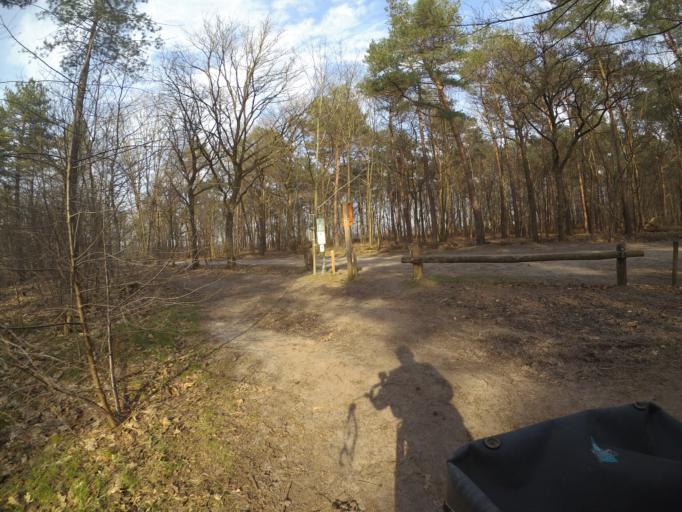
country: NL
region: North Brabant
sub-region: Gemeente Dongen
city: Dongen
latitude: 51.6028
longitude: 4.9023
